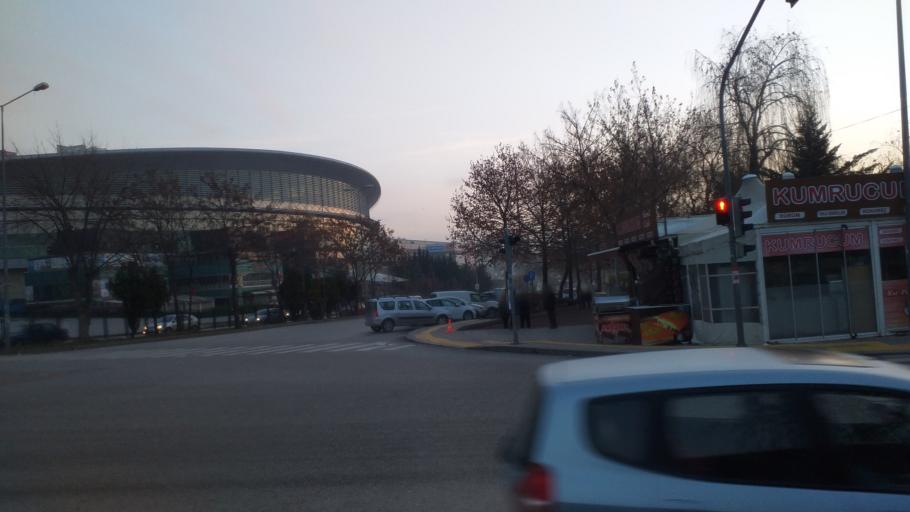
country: TR
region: Ankara
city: Ankara
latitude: 39.9686
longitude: 32.8189
